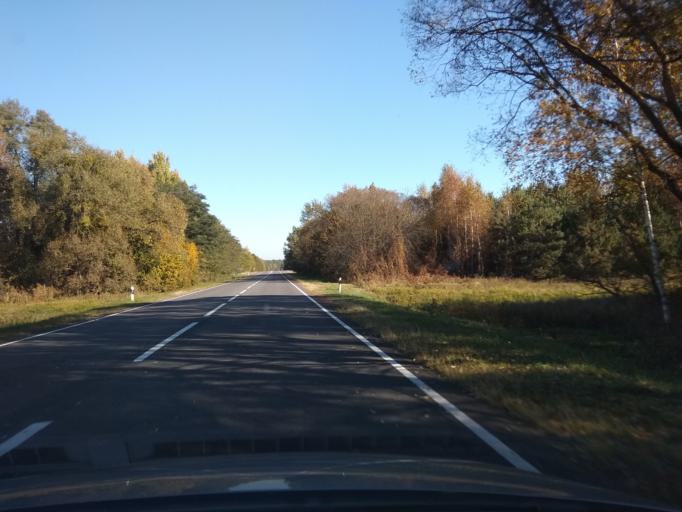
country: BY
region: Brest
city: Kobryn
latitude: 52.0188
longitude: 24.2401
